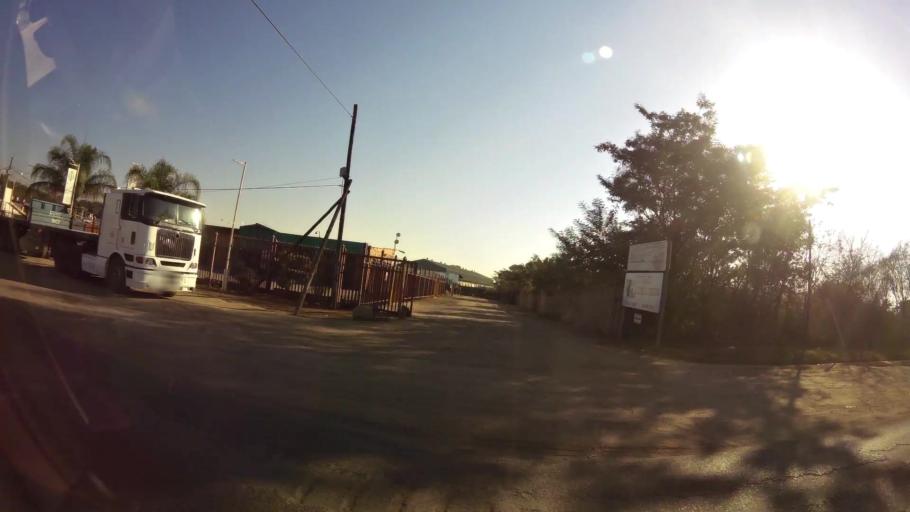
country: ZA
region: Gauteng
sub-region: City of Tshwane Metropolitan Municipality
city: Pretoria
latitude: -25.6535
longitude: 28.1927
